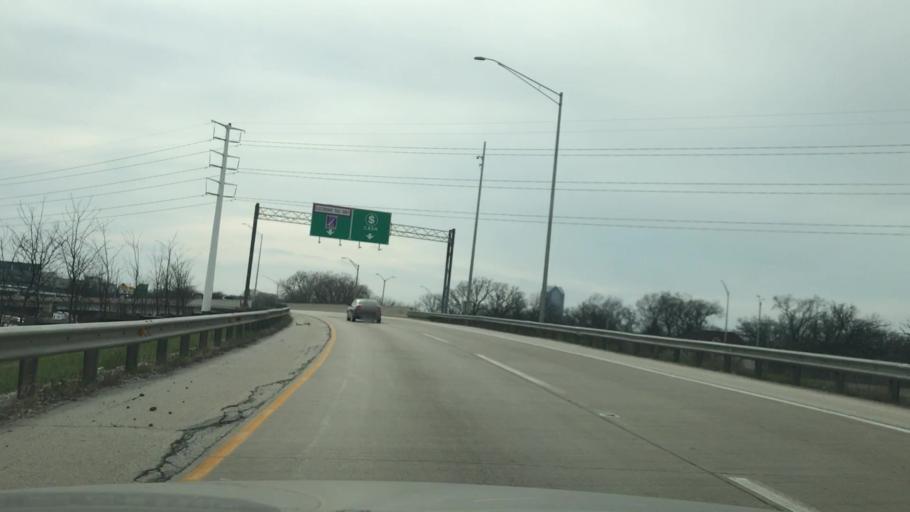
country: US
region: Illinois
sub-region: DuPage County
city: Oak Brook
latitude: 41.8536
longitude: -87.9309
